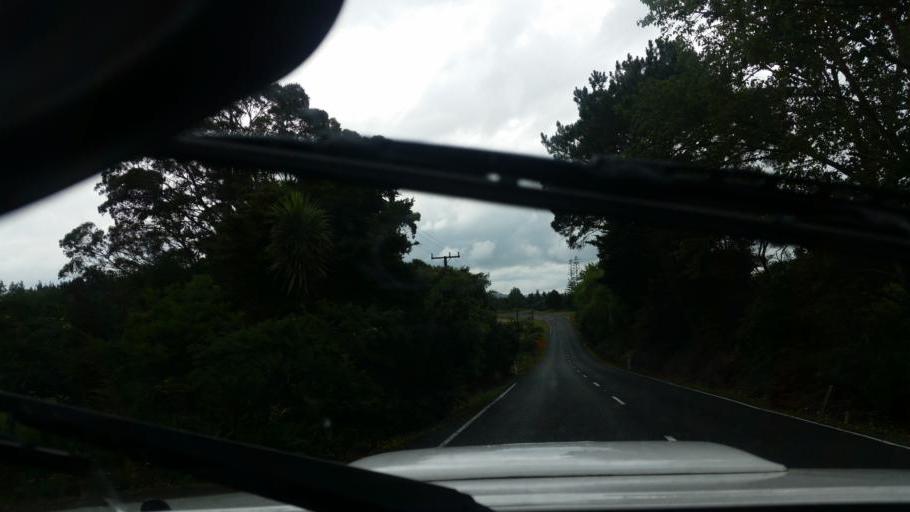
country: NZ
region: Auckland
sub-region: Auckland
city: Wellsford
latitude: -36.1482
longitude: 174.2218
